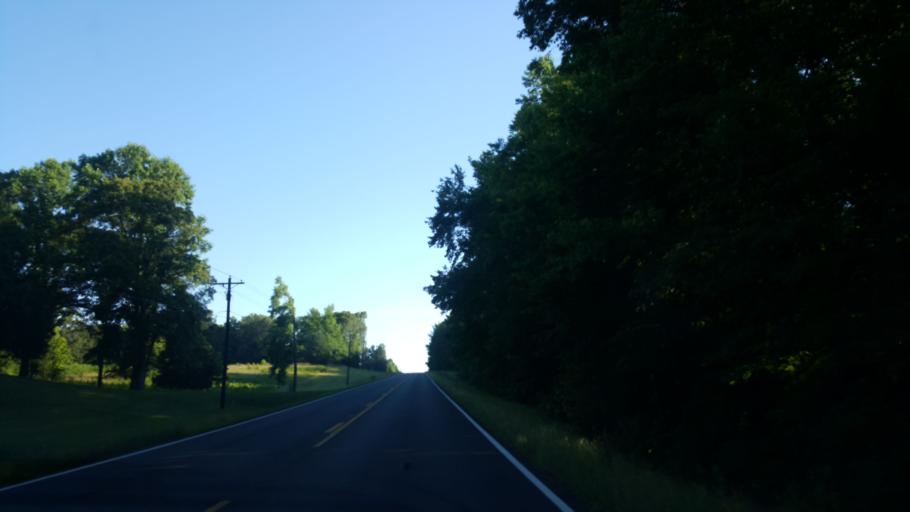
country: US
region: Tennessee
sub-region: Henderson County
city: Lexington
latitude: 35.5346
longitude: -88.3827
